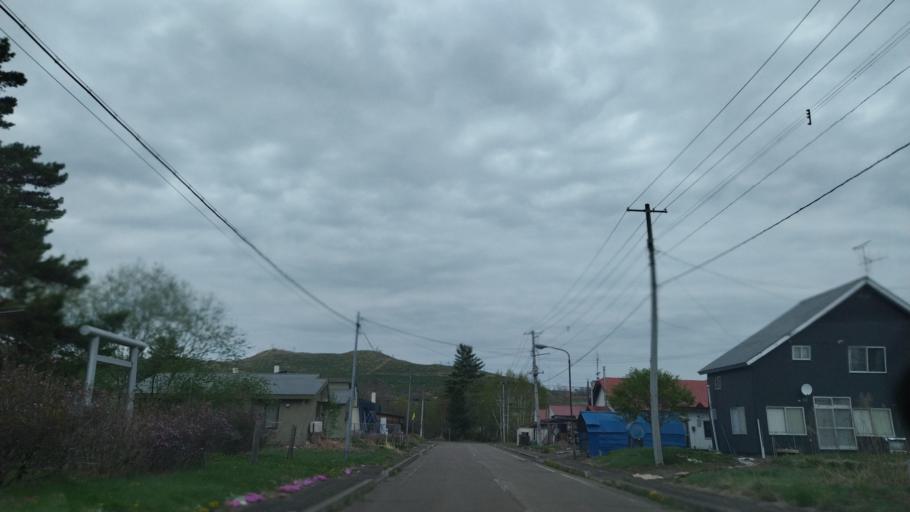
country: JP
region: Hokkaido
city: Kitami
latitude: 43.3532
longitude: 143.6047
